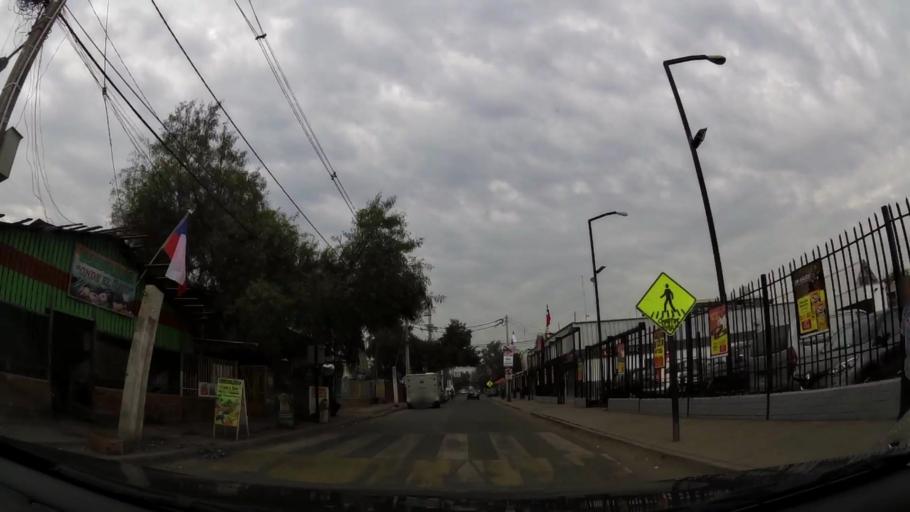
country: CL
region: Santiago Metropolitan
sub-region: Provincia de Chacabuco
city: Lampa
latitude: -33.2314
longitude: -70.8075
